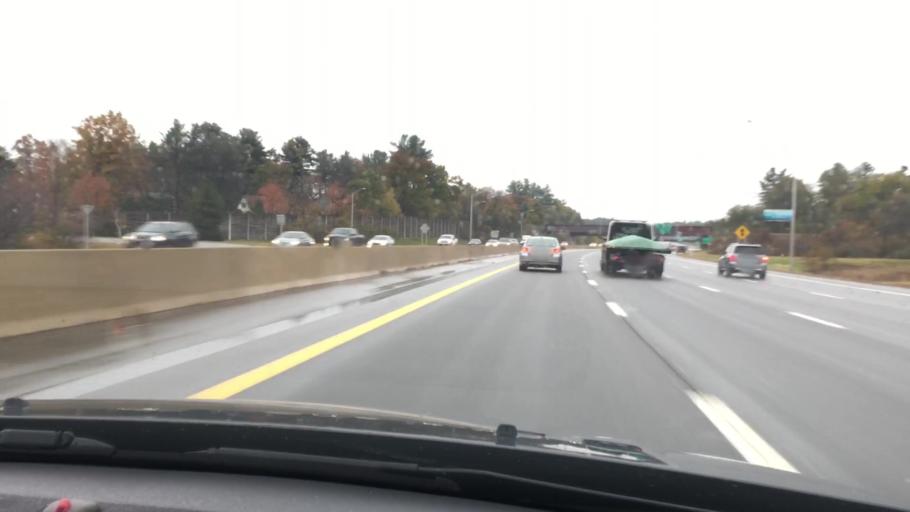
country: US
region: New Hampshire
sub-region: Hillsborough County
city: Nashua
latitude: 42.7761
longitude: -71.4930
